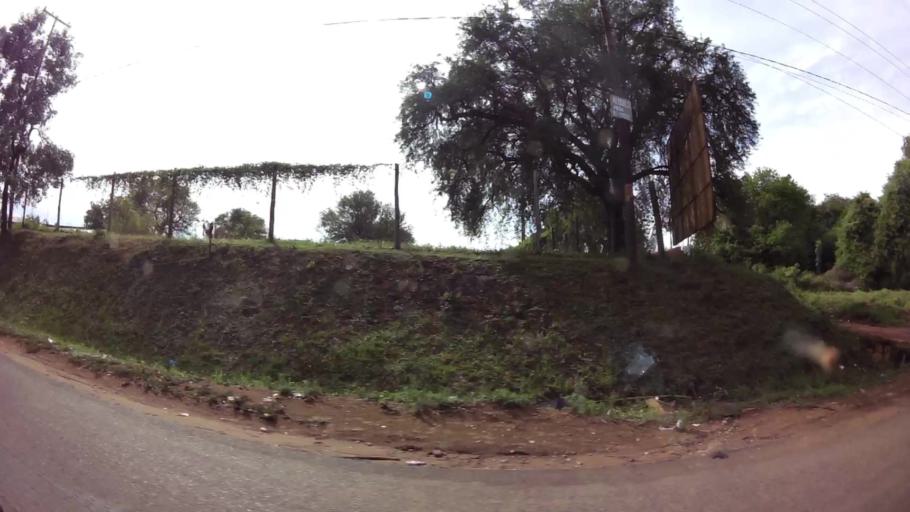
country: PY
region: Central
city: Limpio
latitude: -25.1602
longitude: -57.4654
